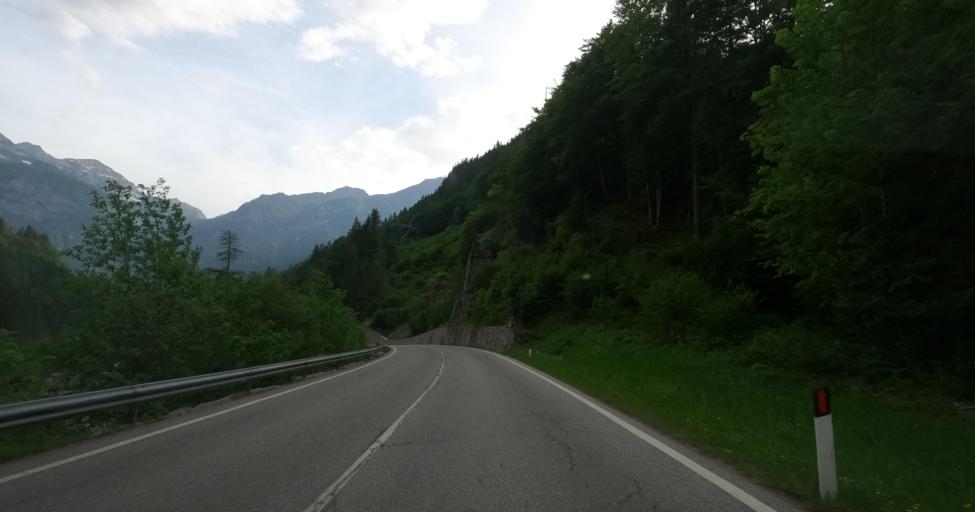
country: IT
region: Veneto
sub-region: Provincia di Belluno
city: Cencenighe Agordino
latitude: 46.3632
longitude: 11.9748
